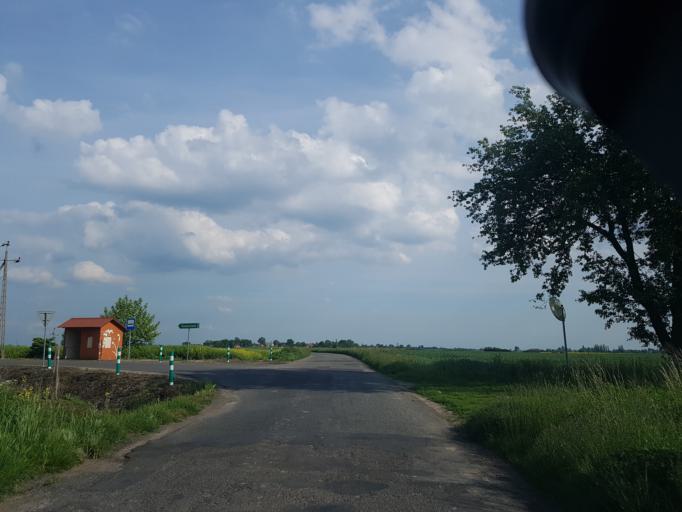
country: PL
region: Lower Silesian Voivodeship
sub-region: Powiat olawski
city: Wierzbno
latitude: 50.8775
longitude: 17.1462
